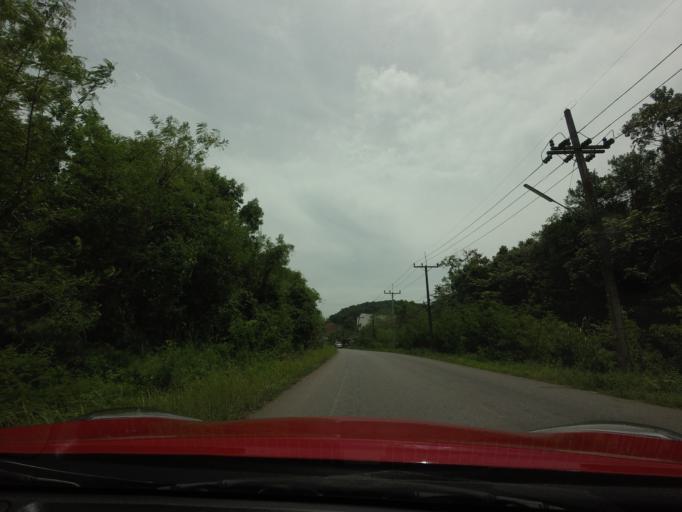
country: TH
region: Songkhla
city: Hat Yai
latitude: 7.0000
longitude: 100.5178
